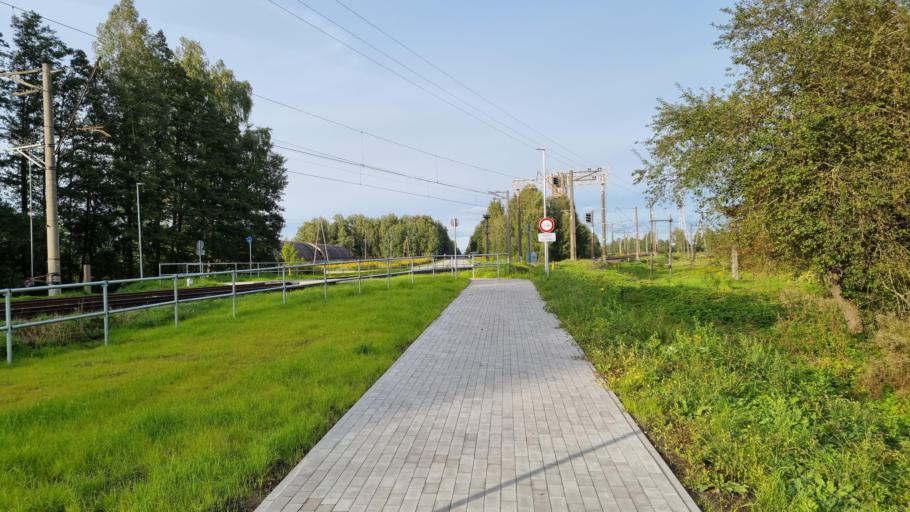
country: LV
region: Olaine
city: Olaine
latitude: 56.8133
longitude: 24.0022
